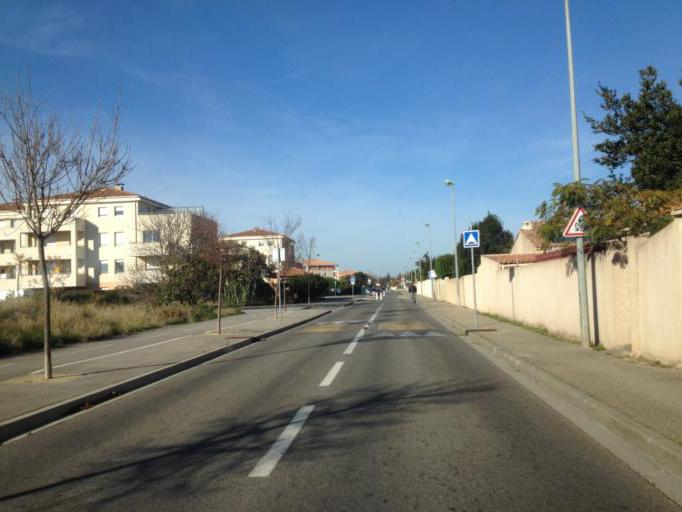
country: FR
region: Provence-Alpes-Cote d'Azur
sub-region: Departement des Bouches-du-Rhone
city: Istres
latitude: 43.5104
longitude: 4.9676
